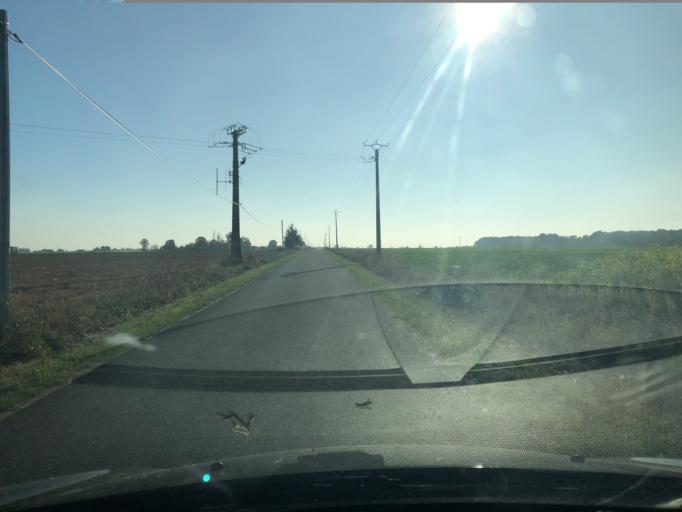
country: FR
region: Centre
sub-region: Departement d'Indre-et-Loire
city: Neuvy-le-Roi
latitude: 47.6438
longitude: 0.6124
